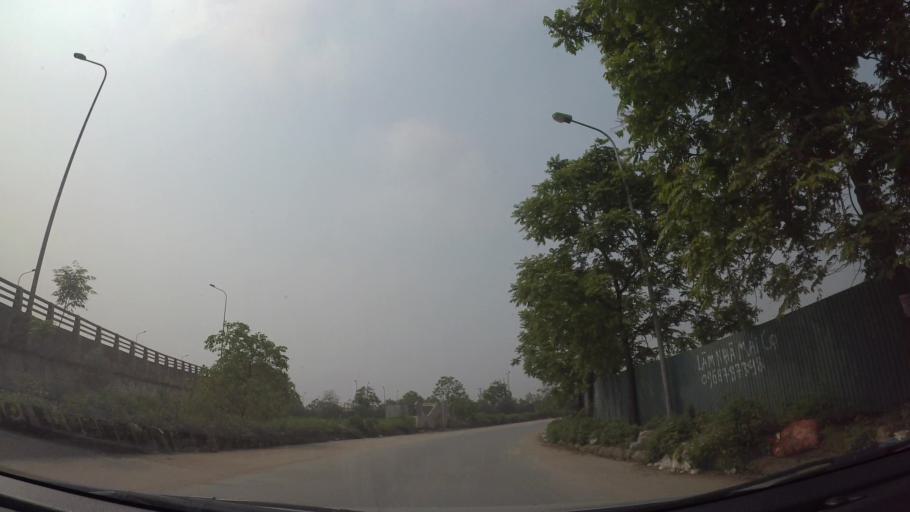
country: VN
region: Ha Noi
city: Cau Dien
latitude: 21.0106
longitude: 105.7470
